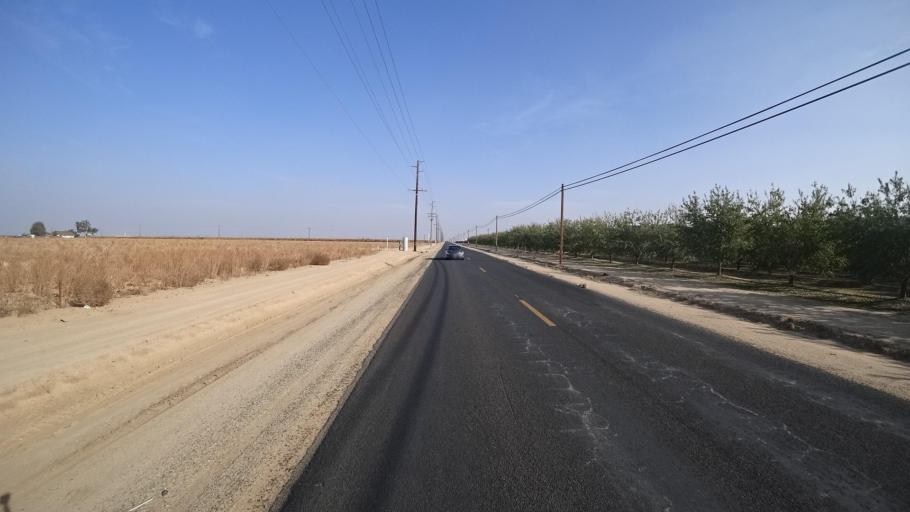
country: US
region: California
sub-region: Tulare County
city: Richgrove
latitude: 35.7761
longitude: -119.1370
